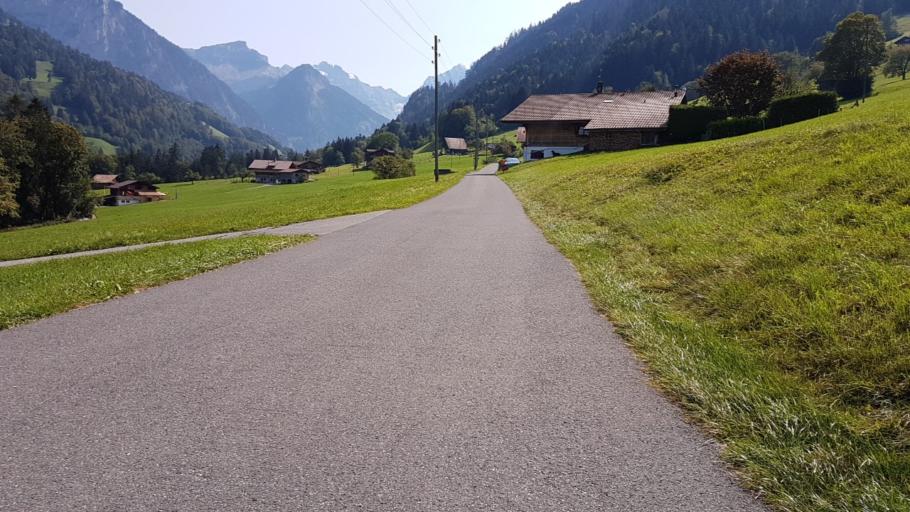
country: CH
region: Bern
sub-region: Frutigen-Niedersimmental District
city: Frutigen
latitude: 46.6096
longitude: 7.6897
